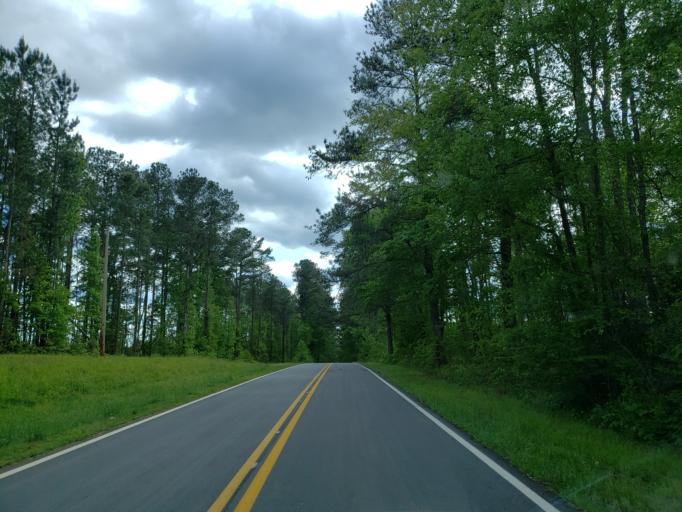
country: US
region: Georgia
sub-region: Carroll County
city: Mount Zion
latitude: 33.6744
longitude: -85.2301
